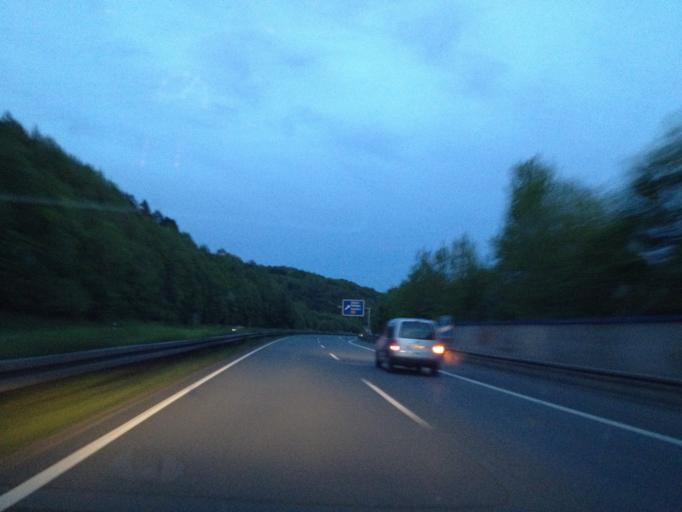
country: DE
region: North Rhine-Westphalia
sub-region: Regierungsbezirk Arnsberg
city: Sundern
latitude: 51.4404
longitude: 7.9845
